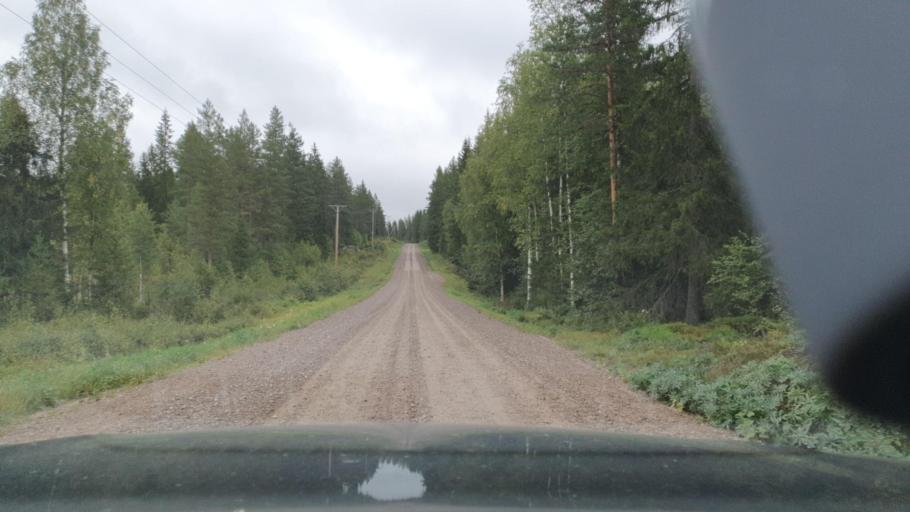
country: SE
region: Vaermland
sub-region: Torsby Kommun
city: Torsby
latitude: 60.4801
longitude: 12.9131
